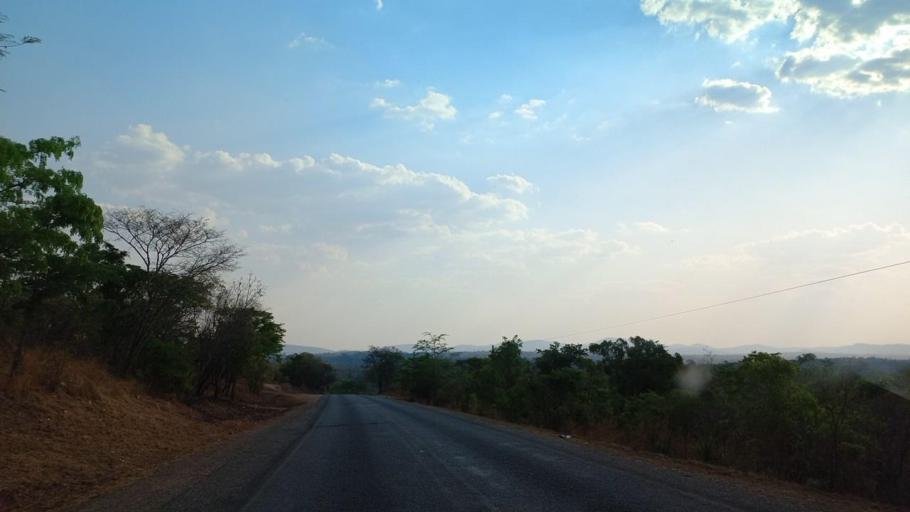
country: ZM
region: Lusaka
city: Luangwa
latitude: -15.0211
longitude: 29.9529
